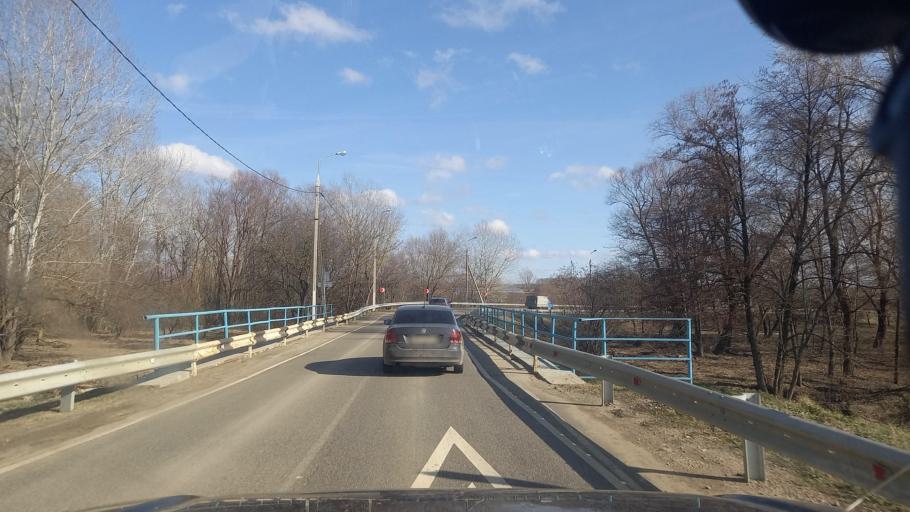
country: RU
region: Krasnodarskiy
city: Novodmitriyevskaya
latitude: 44.7771
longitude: 38.9750
